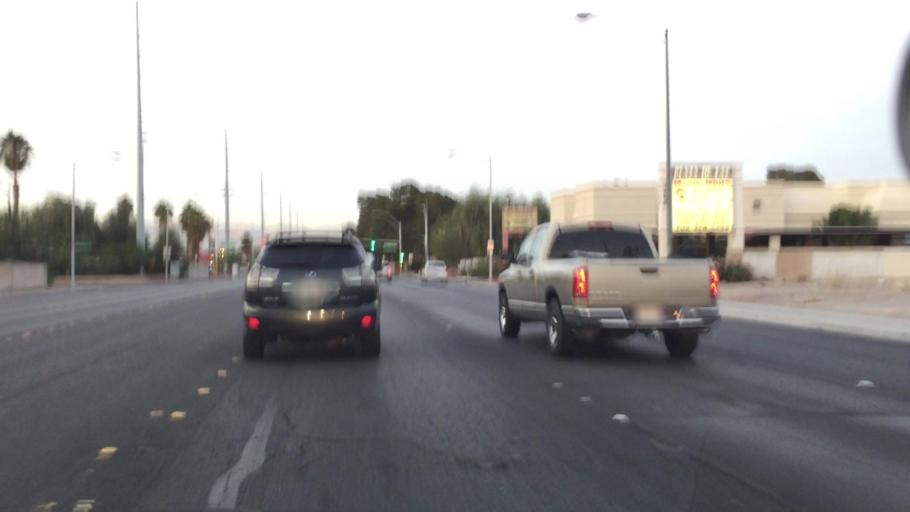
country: US
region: Nevada
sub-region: Clark County
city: Paradise
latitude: 36.0951
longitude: -115.1189
